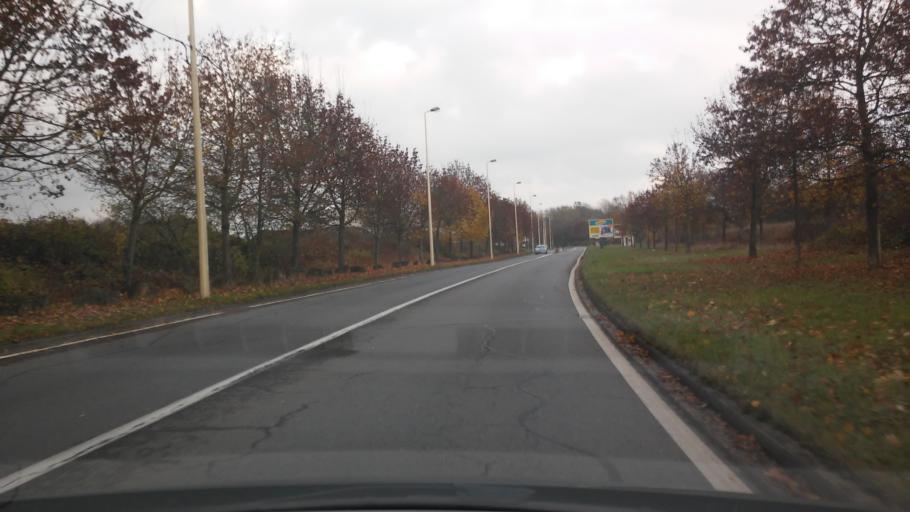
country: FR
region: Lorraine
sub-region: Departement de la Moselle
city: Terville
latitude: 49.3344
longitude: 6.1554
